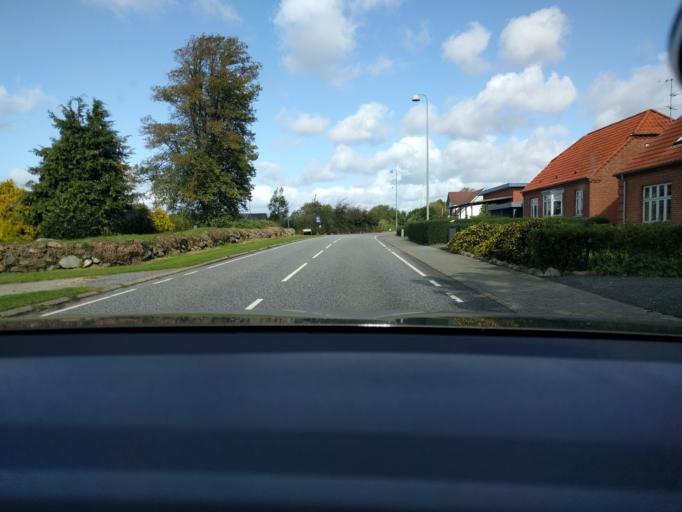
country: DK
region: Central Jutland
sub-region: Viborg Kommune
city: Bjerringbro
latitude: 56.3054
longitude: 9.7167
